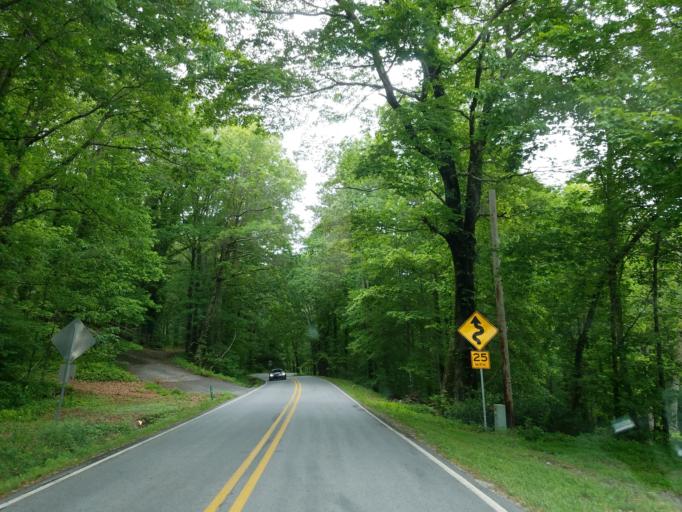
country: US
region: Georgia
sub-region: Union County
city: Blairsville
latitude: 34.7078
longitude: -83.9972
